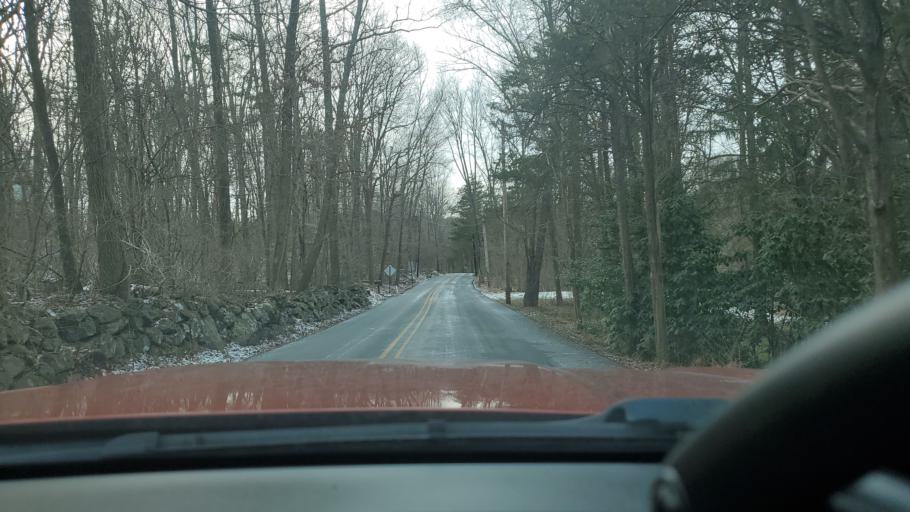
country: US
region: Pennsylvania
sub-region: Montgomery County
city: Red Hill
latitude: 40.3277
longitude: -75.5107
